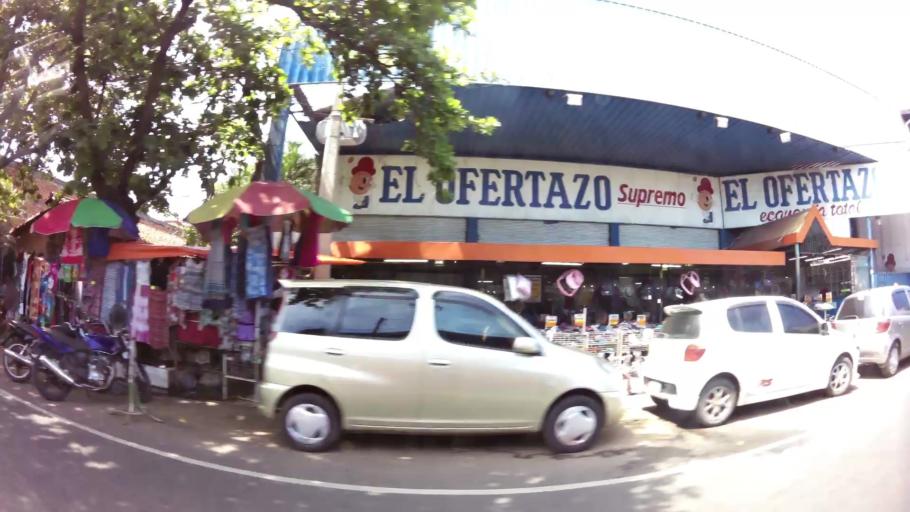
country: PY
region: Central
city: San Lorenzo
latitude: -25.3460
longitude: -57.5127
